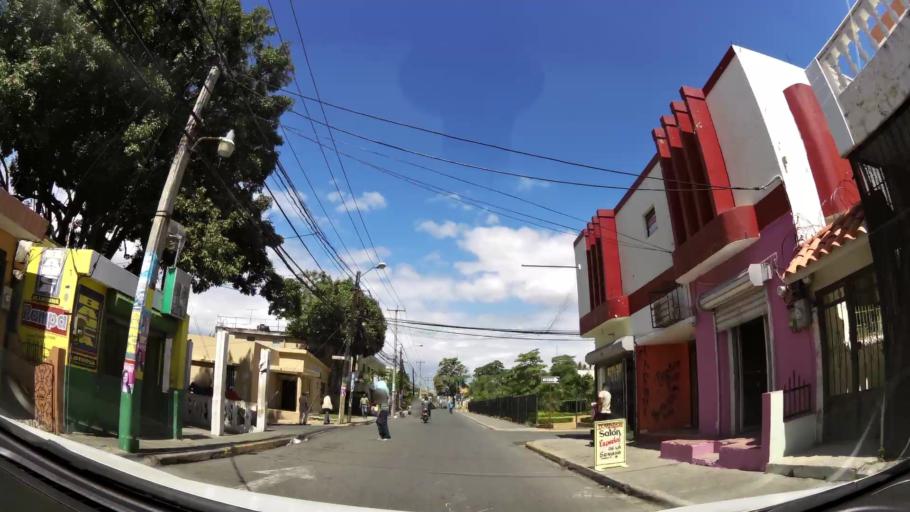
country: DO
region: San Cristobal
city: San Cristobal
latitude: 18.4129
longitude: -70.1093
